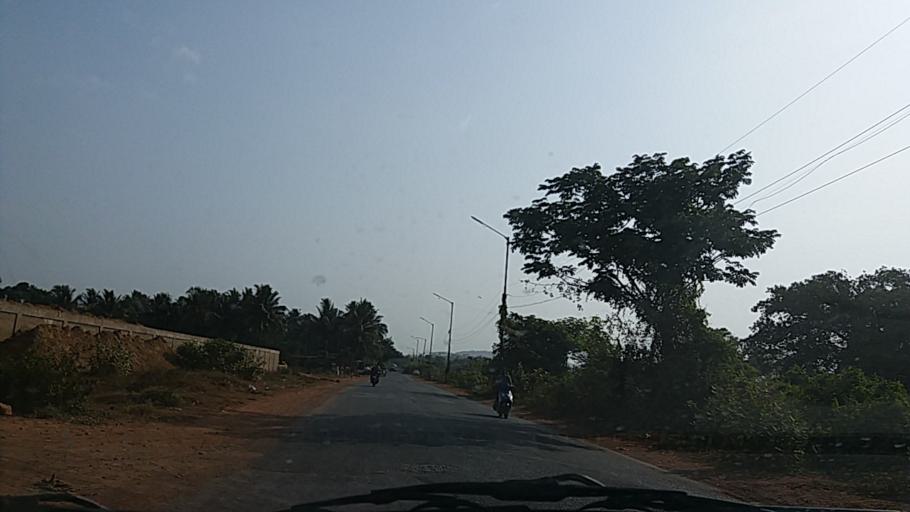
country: IN
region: Goa
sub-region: South Goa
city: Madgaon
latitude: 15.2605
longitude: 73.9688
